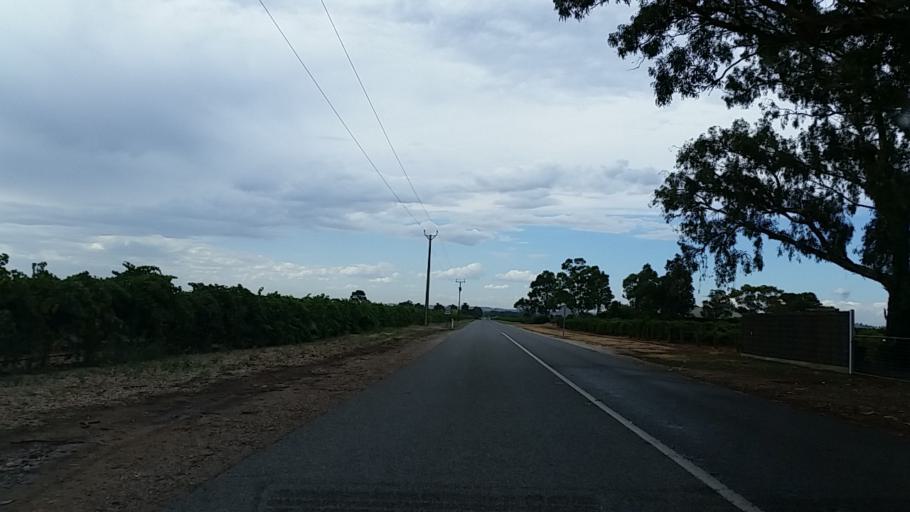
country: AU
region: South Australia
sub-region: Barossa
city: Nuriootpa
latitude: -34.4901
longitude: 139.0153
